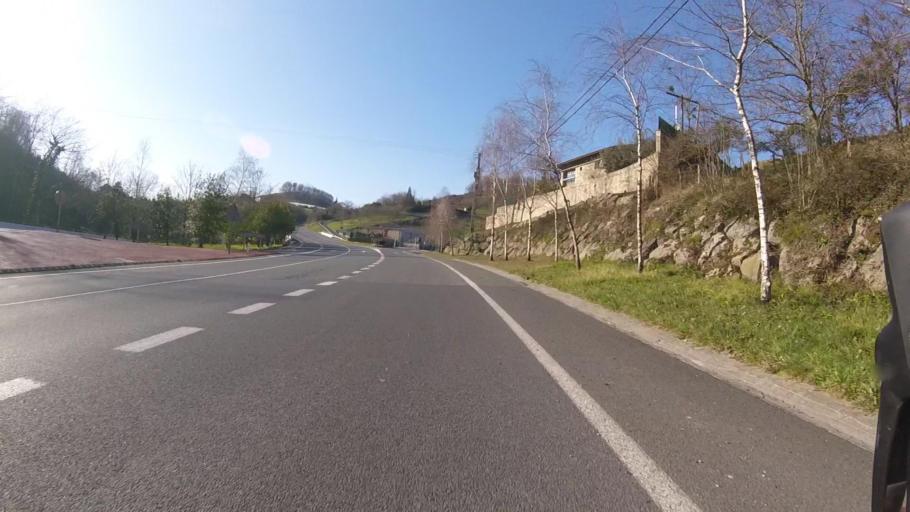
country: ES
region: Basque Country
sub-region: Provincia de Guipuzcoa
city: Astigarraga
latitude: 43.2863
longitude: -1.9333
